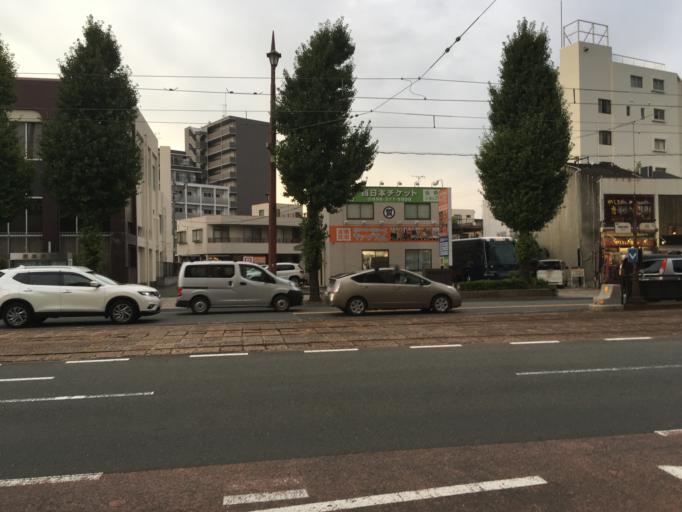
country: JP
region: Kumamoto
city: Kumamoto
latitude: 32.7957
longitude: 130.7232
